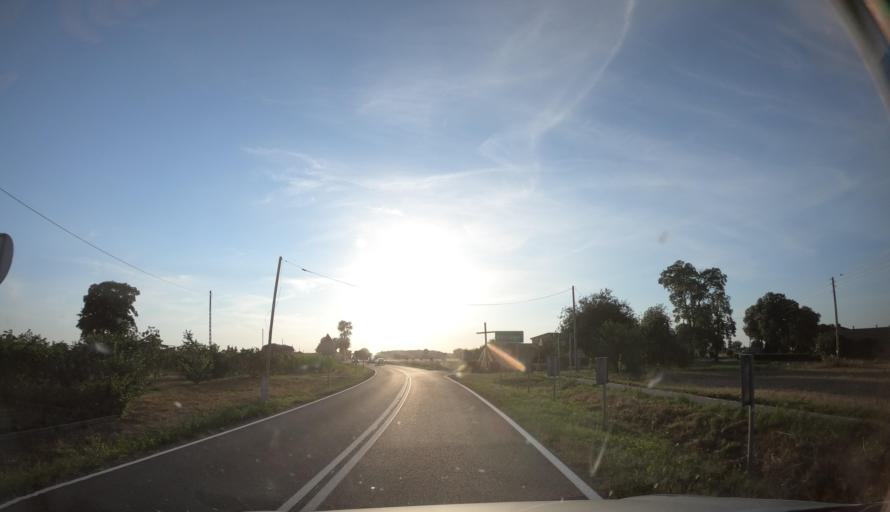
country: PL
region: Kujawsko-Pomorskie
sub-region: Powiat swiecki
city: Pruszcz
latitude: 53.3038
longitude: 18.0983
